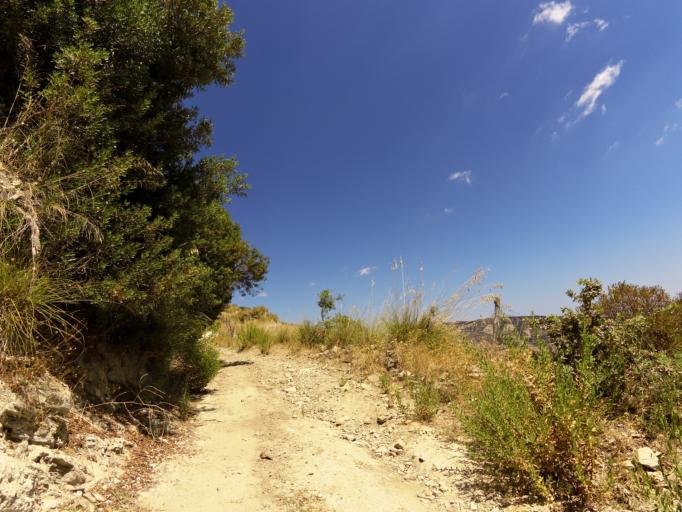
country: IT
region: Calabria
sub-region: Provincia di Reggio Calabria
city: Stilo
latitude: 38.4601
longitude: 16.4625
